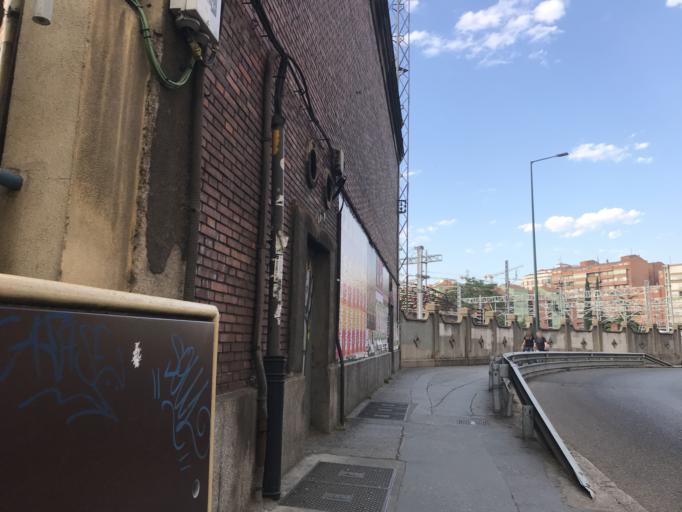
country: ES
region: Castille and Leon
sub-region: Provincia de Valladolid
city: Valladolid
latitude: 41.6416
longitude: -4.7291
